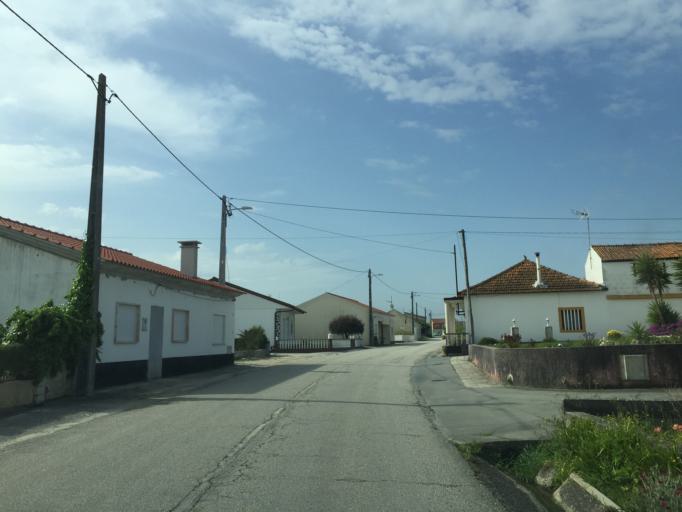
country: PT
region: Coimbra
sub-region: Figueira da Foz
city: Lavos
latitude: 40.0167
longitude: -8.8230
